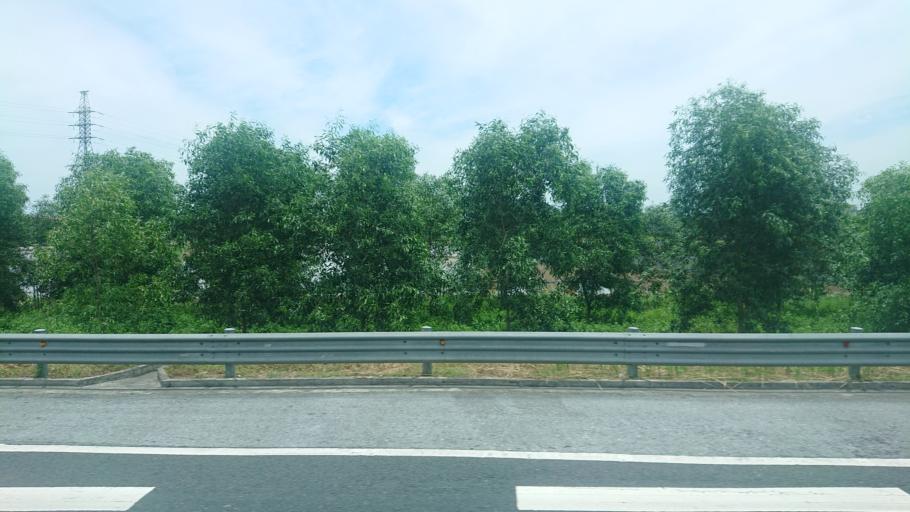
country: VN
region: Hai Phong
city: An Lao
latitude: 20.8017
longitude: 106.5298
